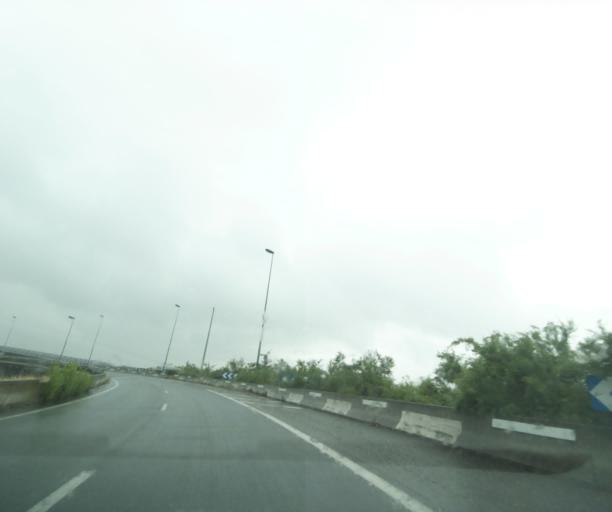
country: FR
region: Midi-Pyrenees
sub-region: Departement de la Haute-Garonne
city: Ramonville-Saint-Agne
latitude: 43.5554
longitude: 1.4911
